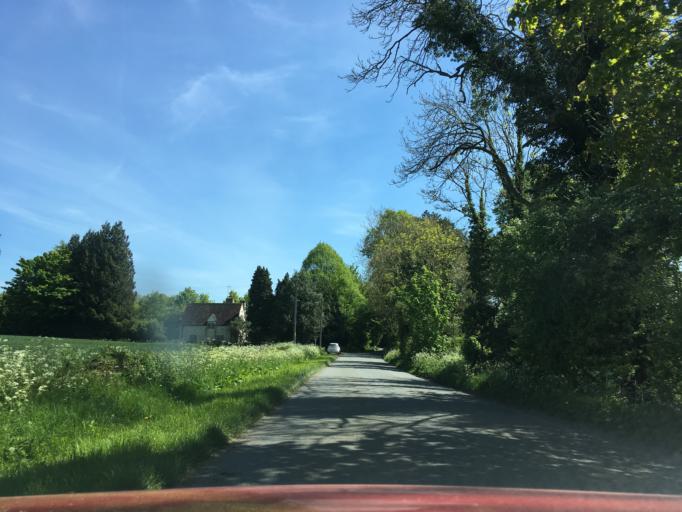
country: GB
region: England
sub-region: Gloucestershire
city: Coates
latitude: 51.7003
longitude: -2.0256
